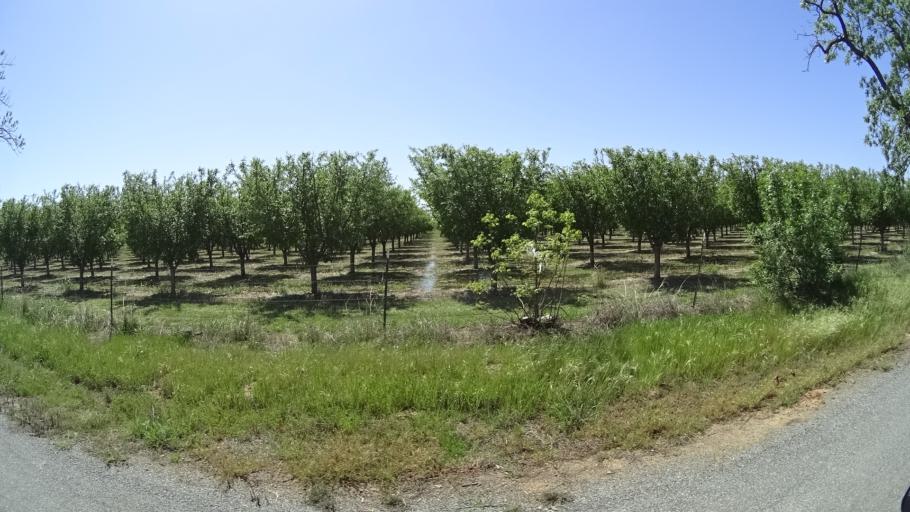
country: US
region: California
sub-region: Glenn County
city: Orland
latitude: 39.7653
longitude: -122.1757
